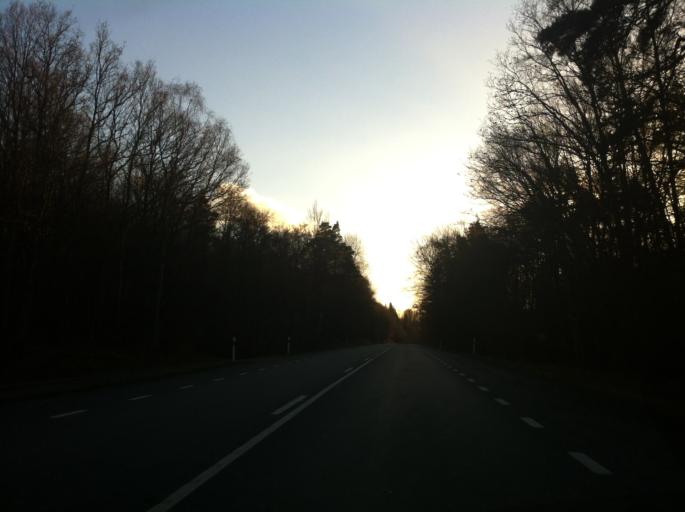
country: SE
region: Skane
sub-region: Hassleholms Kommun
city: Hassleholm
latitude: 56.1506
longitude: 13.8081
